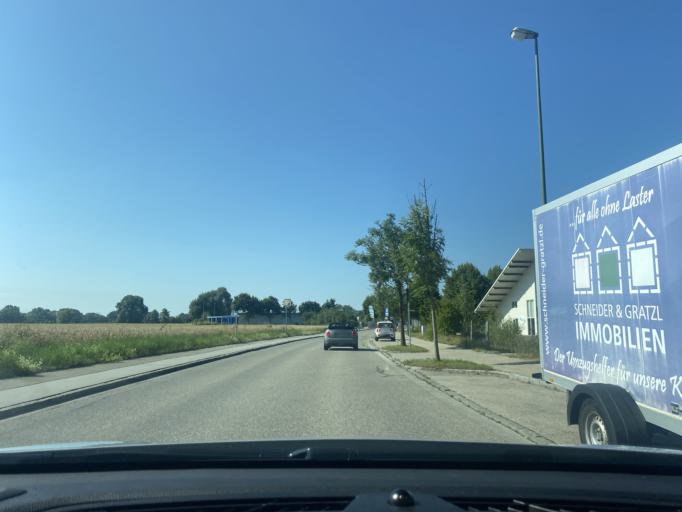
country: DE
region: Bavaria
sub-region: Upper Bavaria
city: Erding
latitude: 48.2784
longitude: 11.9000
